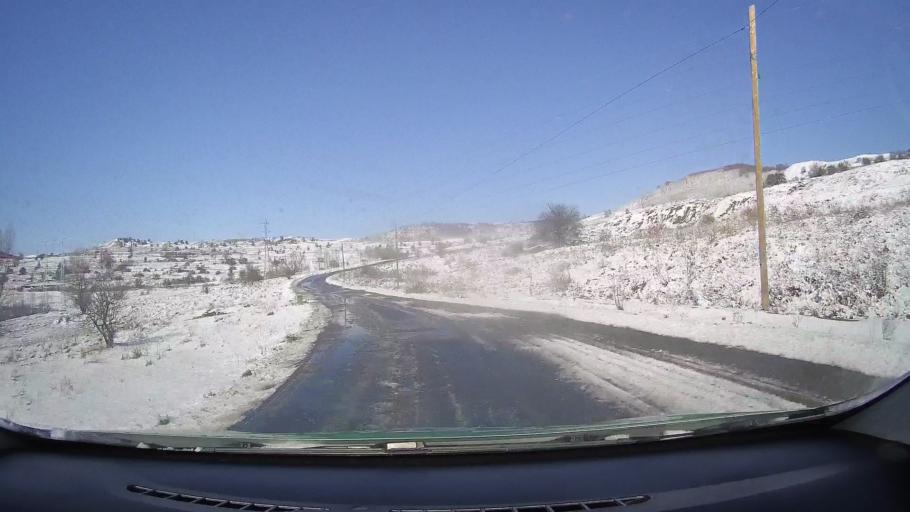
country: RO
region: Sibiu
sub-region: Comuna Avrig
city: Avrig
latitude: 45.7691
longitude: 24.3858
